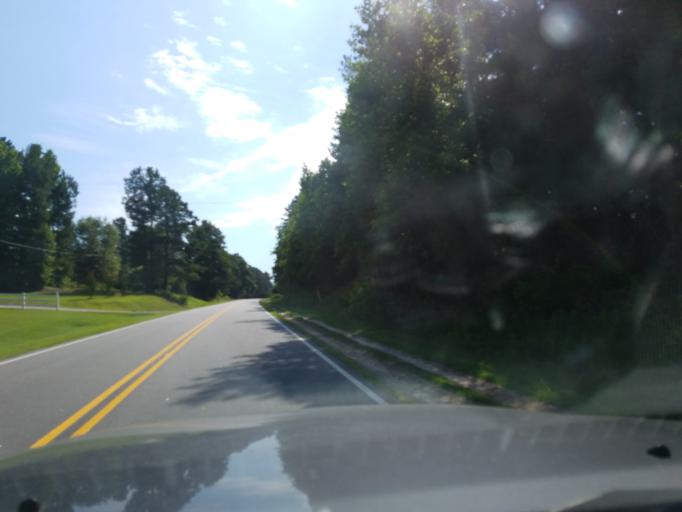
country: US
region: North Carolina
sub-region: Granville County
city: Oxford
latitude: 36.3239
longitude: -78.4990
